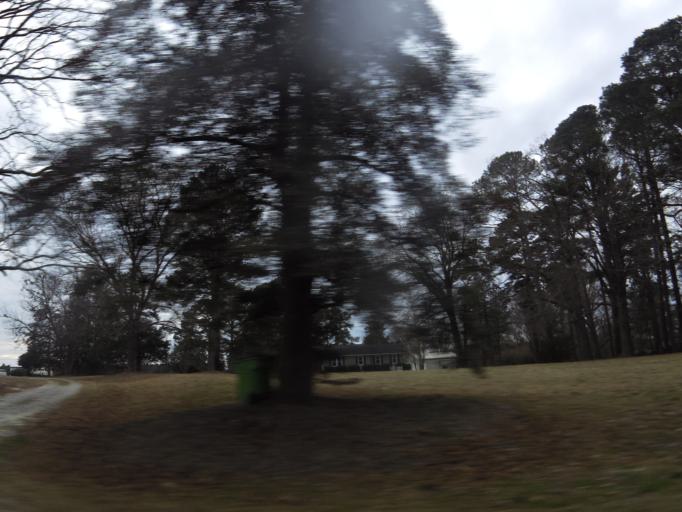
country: US
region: North Carolina
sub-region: Halifax County
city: Scotland Neck
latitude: 36.1452
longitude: -77.4204
